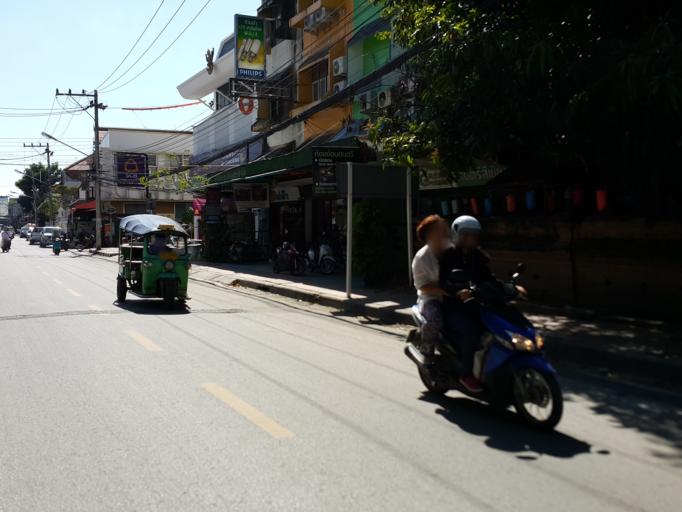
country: TH
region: Chiang Mai
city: Chiang Mai
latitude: 18.7837
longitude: 98.9887
